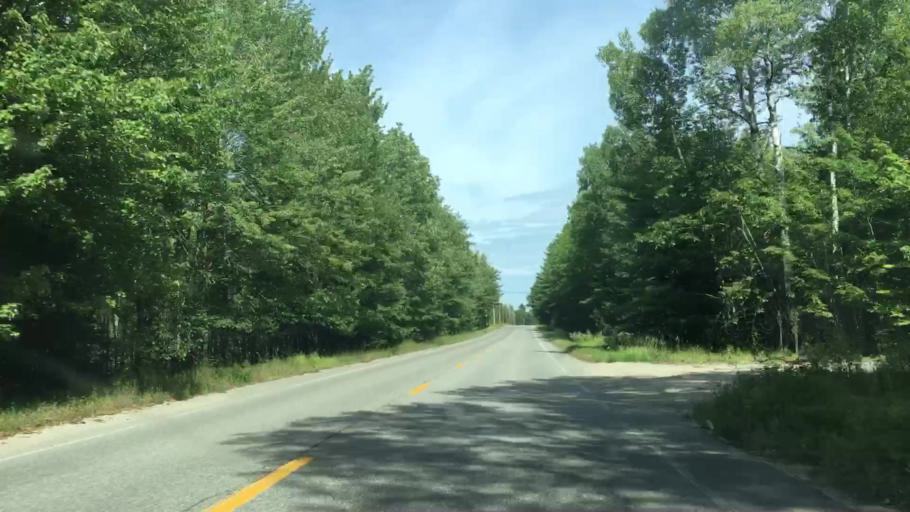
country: US
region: Maine
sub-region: Penobscot County
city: Lincoln
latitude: 45.3879
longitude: -68.5365
